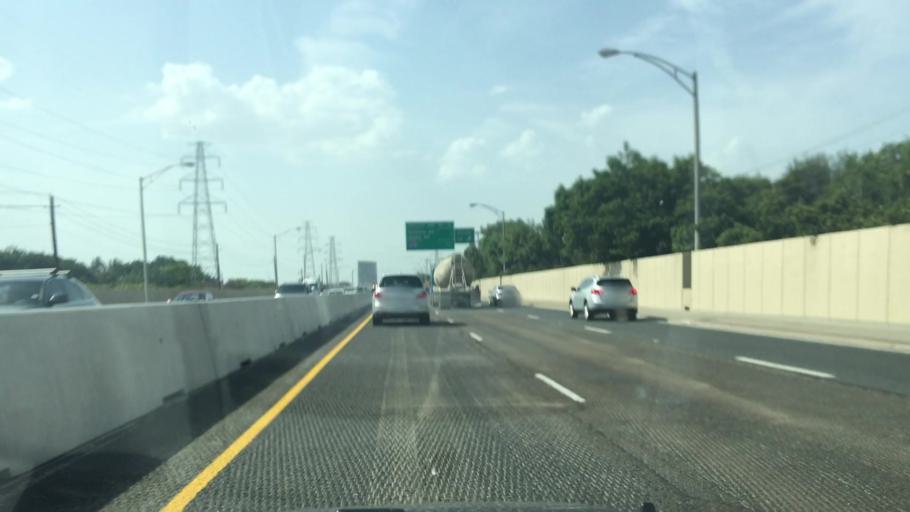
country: US
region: Texas
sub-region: Dallas County
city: University Park
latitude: 32.9051
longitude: -96.8126
